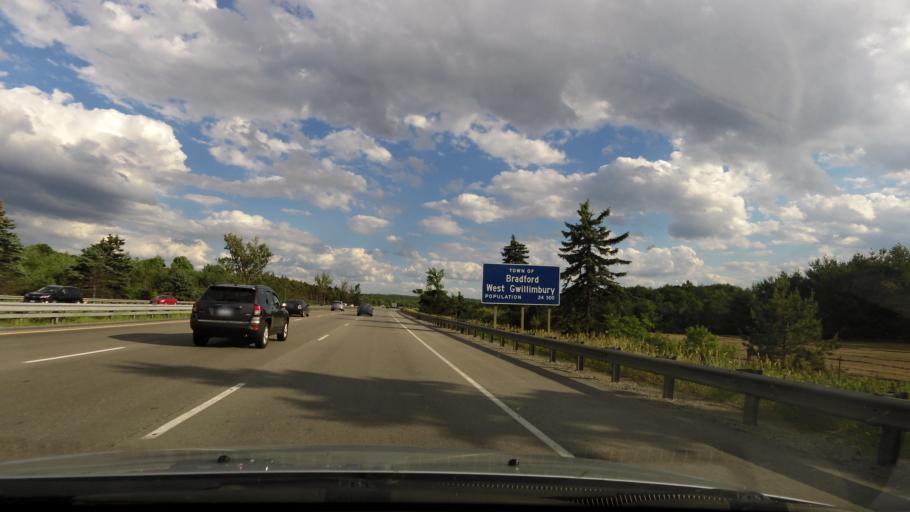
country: CA
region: Ontario
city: Bradford West Gwillimbury
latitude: 44.1824
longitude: -79.6456
